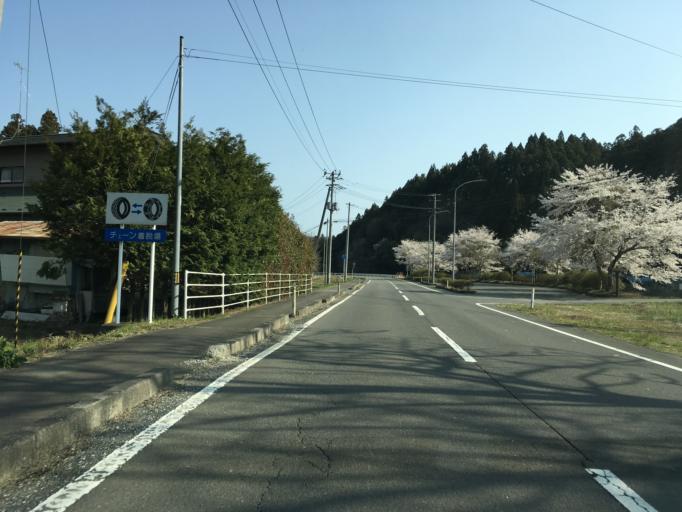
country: JP
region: Iwate
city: Ichinoseki
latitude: 38.7845
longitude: 141.3255
